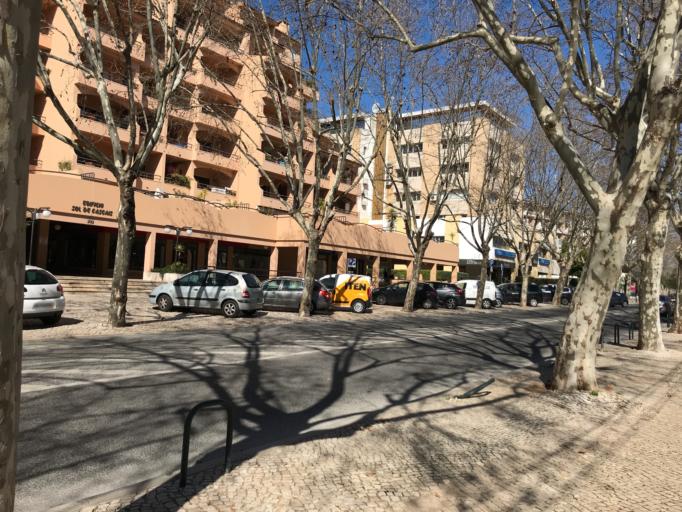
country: PT
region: Lisbon
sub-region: Cascais
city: Cascais
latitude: 38.6990
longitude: -9.4276
